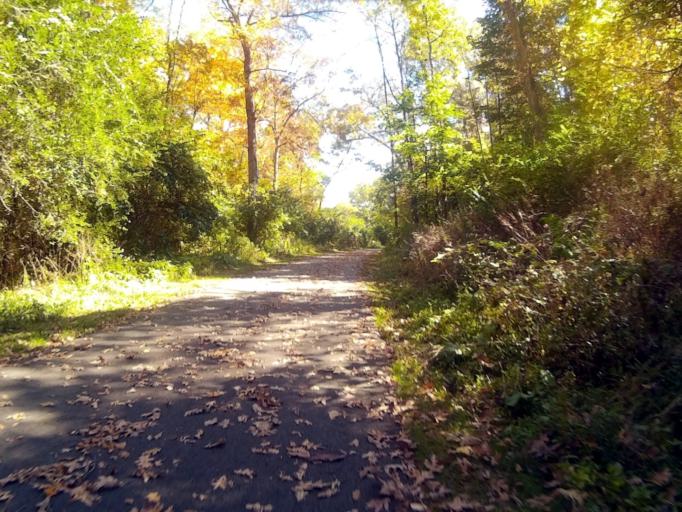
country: US
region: Pennsylvania
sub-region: Centre County
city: State College
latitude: 40.8057
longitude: -77.8756
